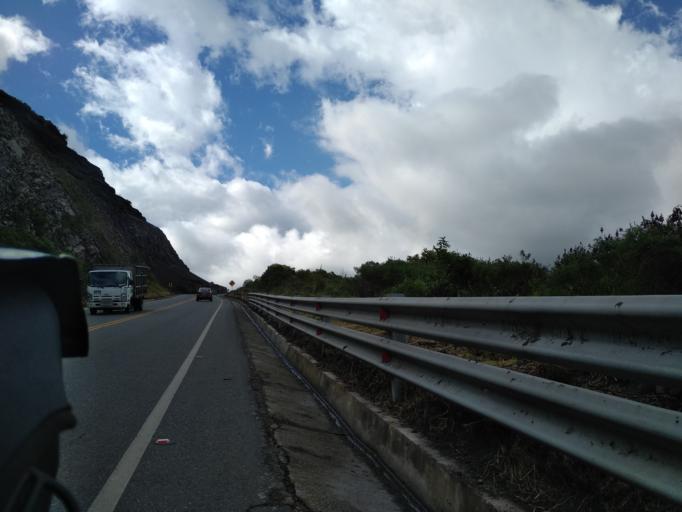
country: EC
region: Tungurahua
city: Banos
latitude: -1.4903
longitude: -78.5173
